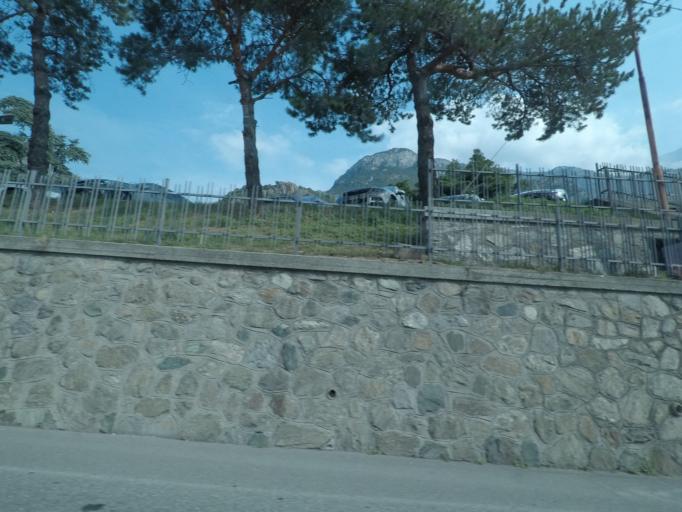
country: IT
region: Aosta Valley
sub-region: Valle d'Aosta
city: Chatillon
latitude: 45.7496
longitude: 7.6175
